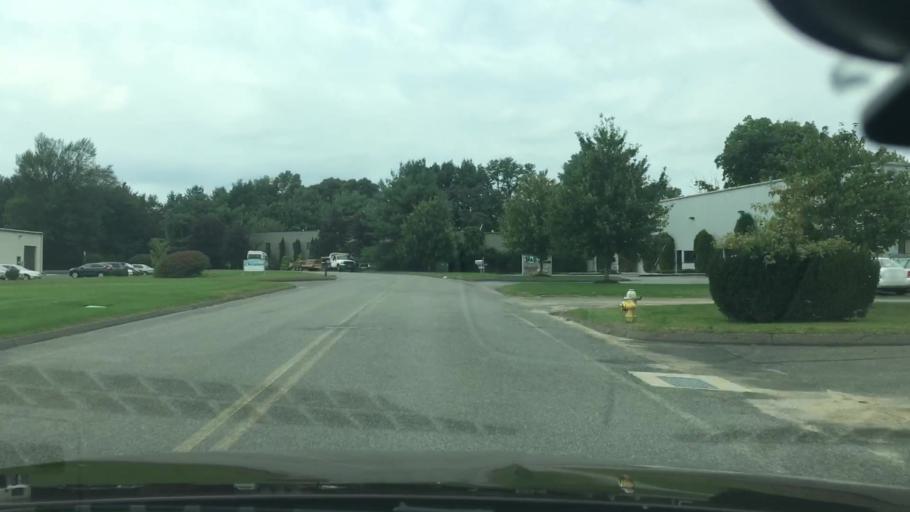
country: US
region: Connecticut
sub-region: Hartford County
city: South Windsor
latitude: 41.8597
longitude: -72.5965
